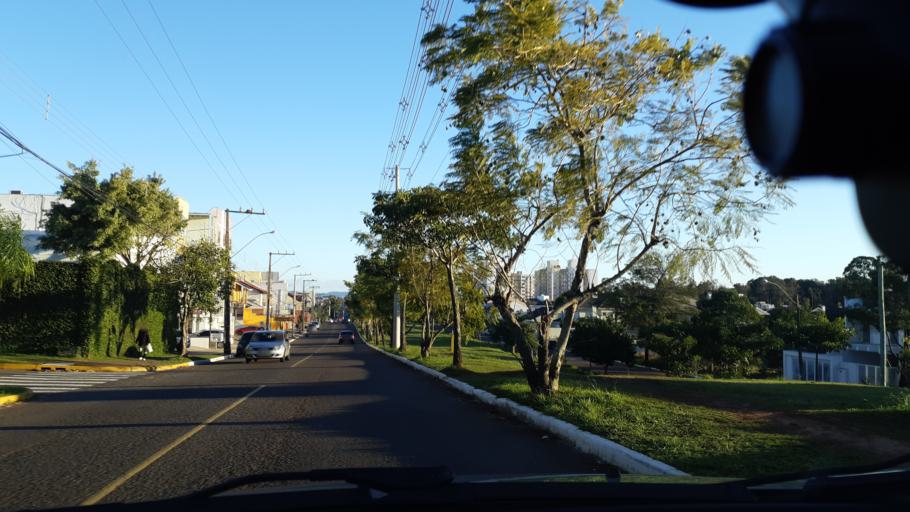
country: BR
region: Rio Grande do Sul
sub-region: Canoas
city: Canoas
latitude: -29.9147
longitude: -51.1542
